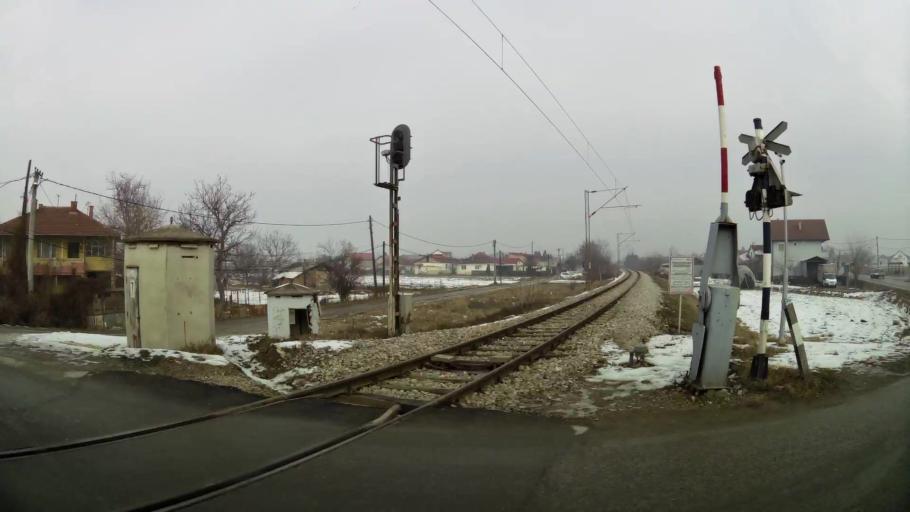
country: MK
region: Ilinden
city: Ilinden
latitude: 41.9952
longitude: 21.5567
